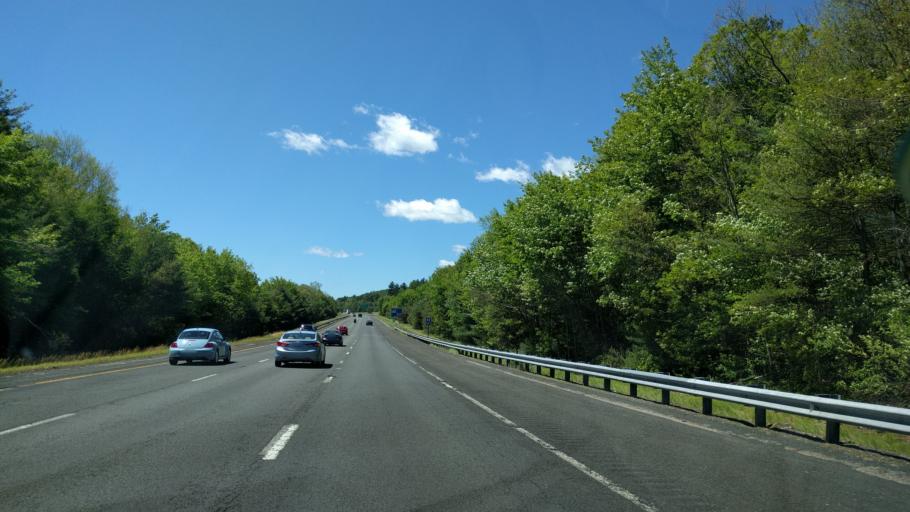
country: US
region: Massachusetts
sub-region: Worcester County
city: Sturbridge
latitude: 42.0749
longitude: -72.1024
